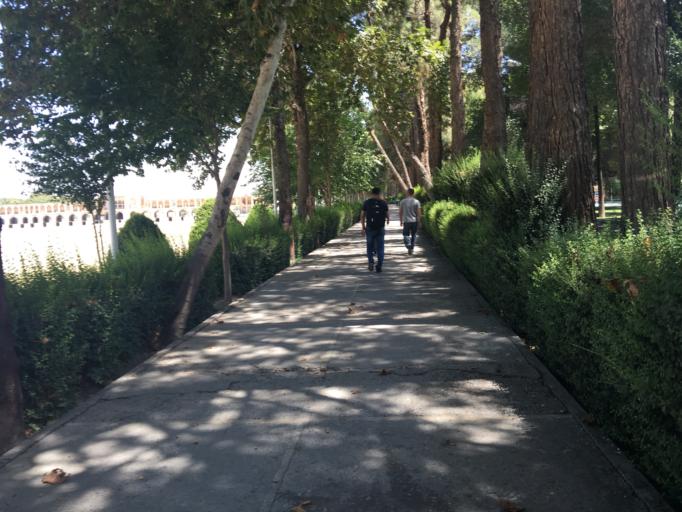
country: IR
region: Isfahan
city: Isfahan
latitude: 32.6358
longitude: 51.6803
